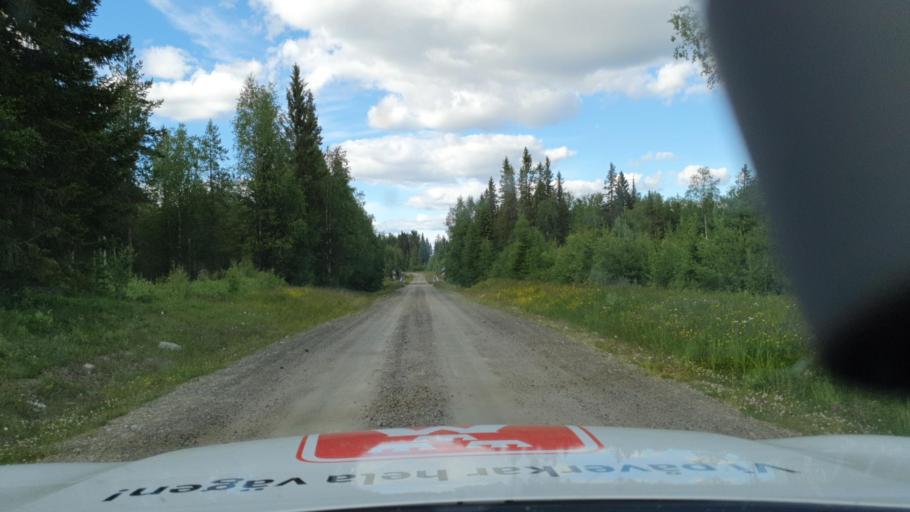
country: SE
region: Vaesterbotten
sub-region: Lycksele Kommun
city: Lycksele
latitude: 64.4517
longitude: 18.3082
